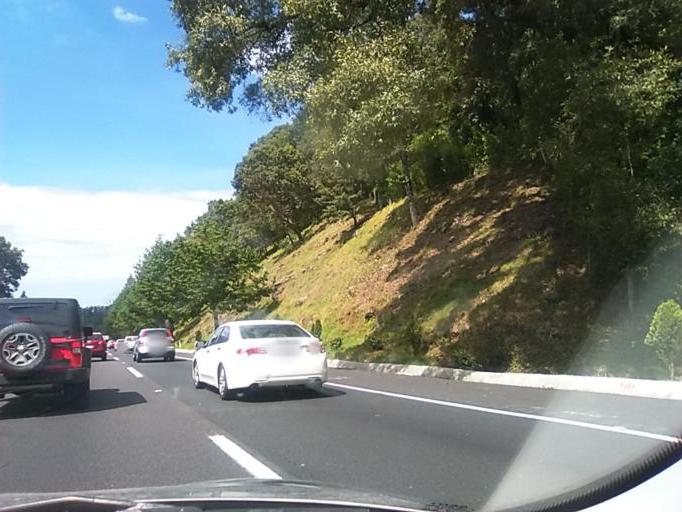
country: MX
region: Morelos
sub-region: Cuernavaca
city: Villa Santiago
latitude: 19.0142
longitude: -99.1582
